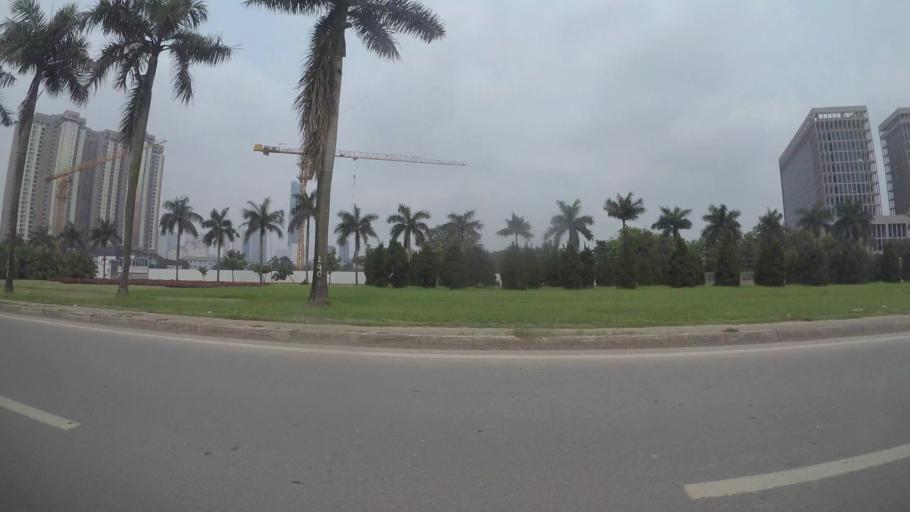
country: VN
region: Ha Noi
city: Thanh Xuan
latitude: 21.0081
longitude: 105.7735
